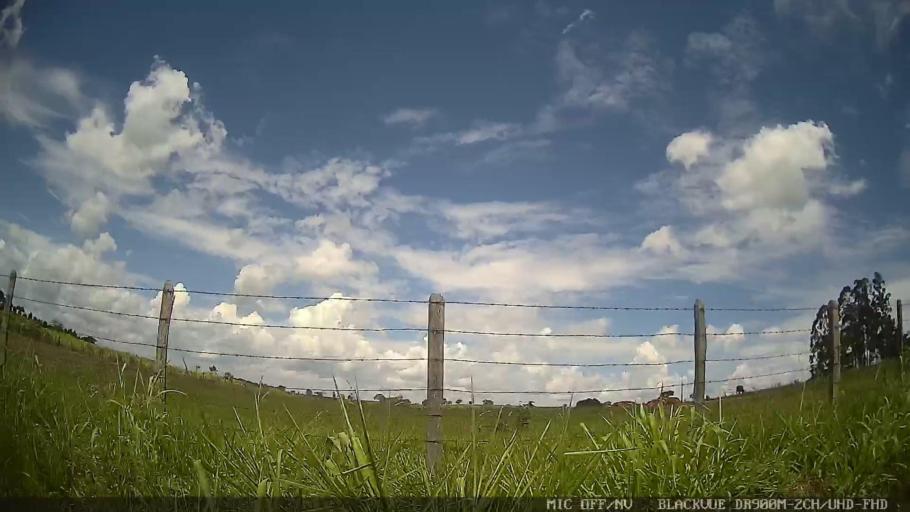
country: BR
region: Sao Paulo
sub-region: Conchas
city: Conchas
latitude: -23.0339
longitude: -47.9954
